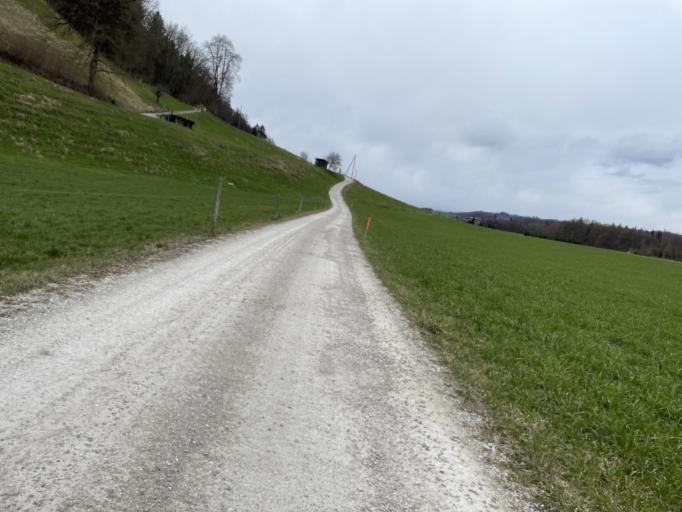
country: CH
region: Bern
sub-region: Bern-Mittelland District
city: Rubigen
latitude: 46.8808
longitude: 7.5309
